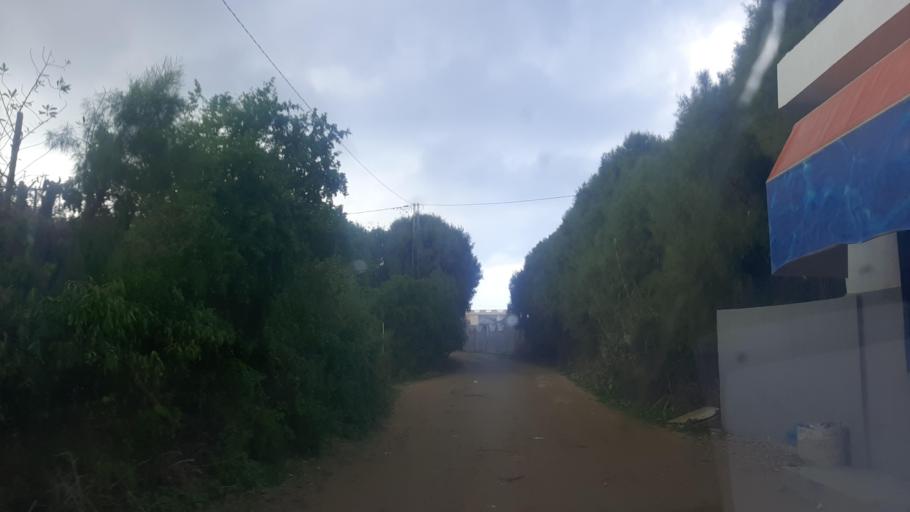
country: TN
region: Nabul
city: Manzil Bu Zalafah
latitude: 36.7368
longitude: 10.5245
